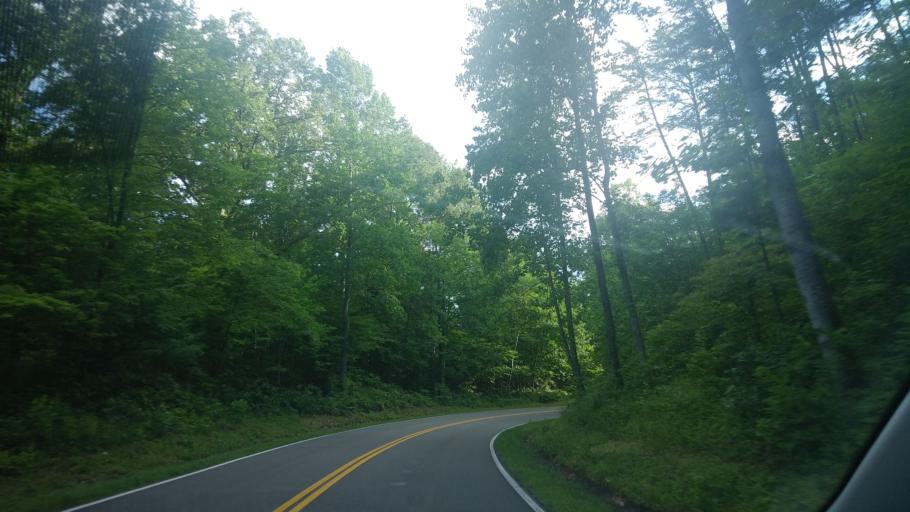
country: US
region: Tennessee
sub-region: Cocke County
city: Newport
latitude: 35.8355
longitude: -83.1925
